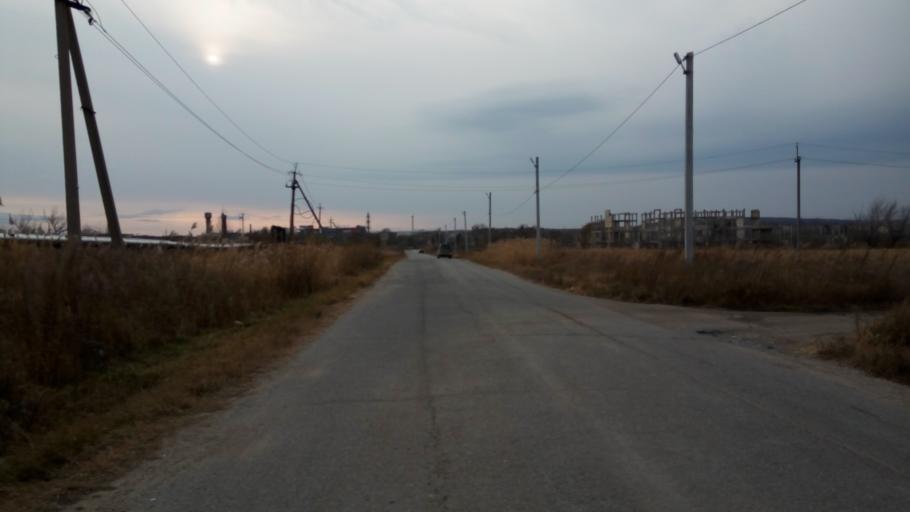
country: RU
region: Primorskiy
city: Novoshakhtinskiy
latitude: 44.0236
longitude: 132.1666
